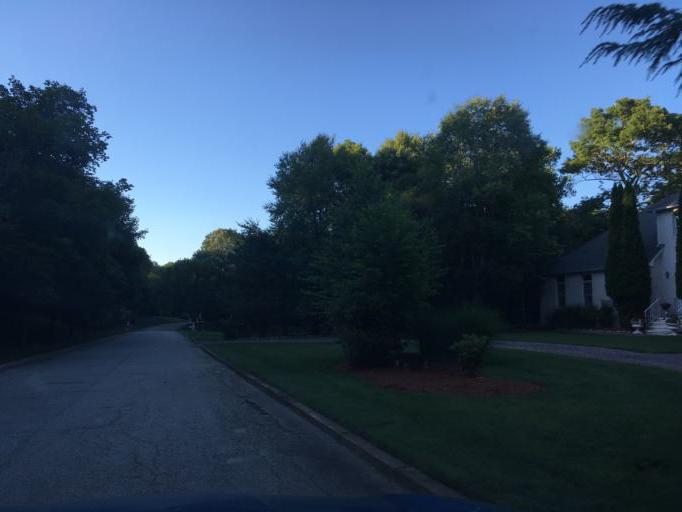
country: US
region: Rhode Island
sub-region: Washington County
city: Exeter
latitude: 41.6194
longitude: -71.5447
